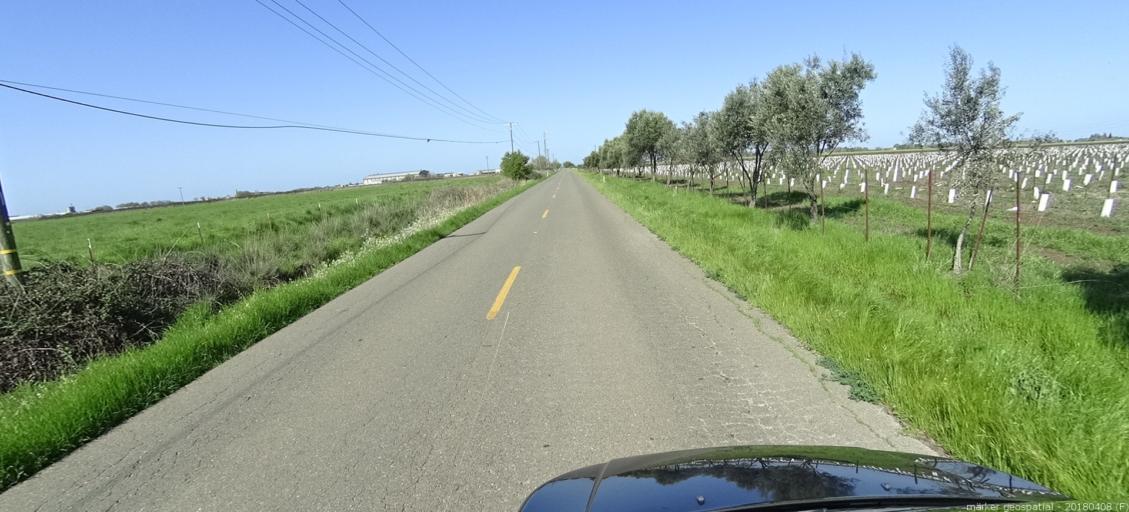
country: US
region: California
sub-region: Sacramento County
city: Elk Grove
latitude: 38.3508
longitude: -121.3868
